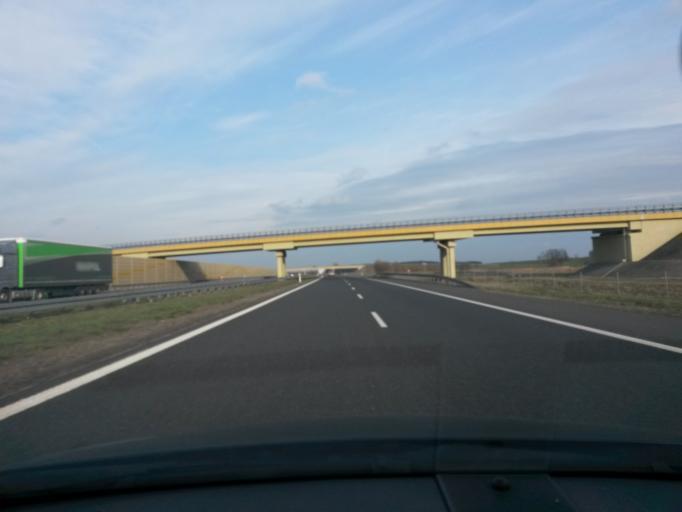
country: PL
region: Lodz Voivodeship
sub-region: Powiat zgierski
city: Parzeczew
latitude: 51.9402
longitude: 19.1997
